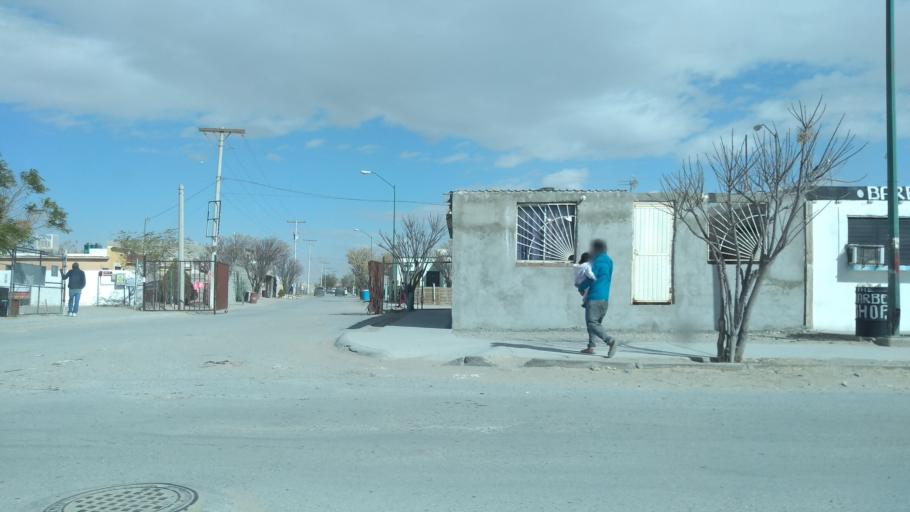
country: US
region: Texas
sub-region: El Paso County
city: San Elizario
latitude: 31.5683
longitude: -106.3420
